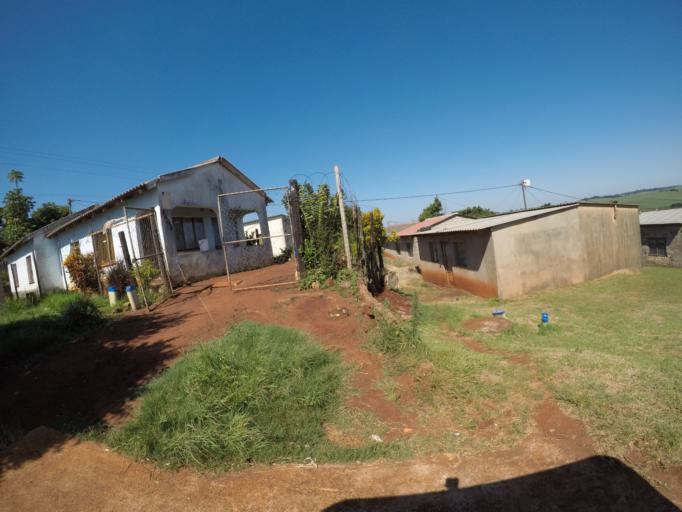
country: ZA
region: KwaZulu-Natal
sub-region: uThungulu District Municipality
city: Empangeni
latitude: -28.7753
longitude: 31.8800
